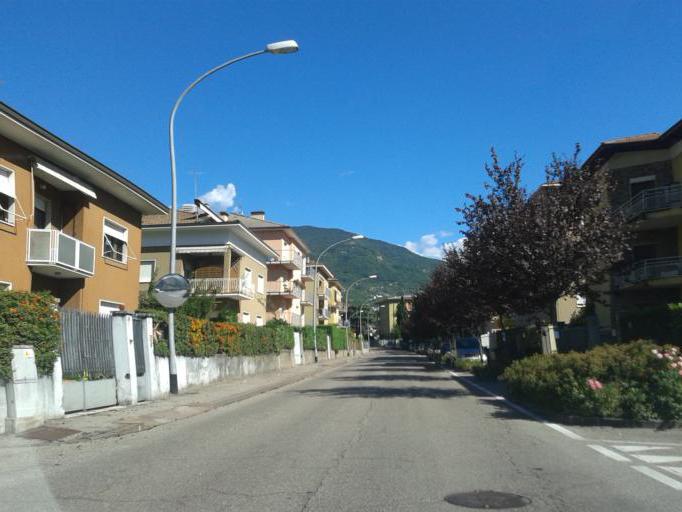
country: IT
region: Trentino-Alto Adige
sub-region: Provincia di Trento
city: Rovereto
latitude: 45.8873
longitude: 11.0284
